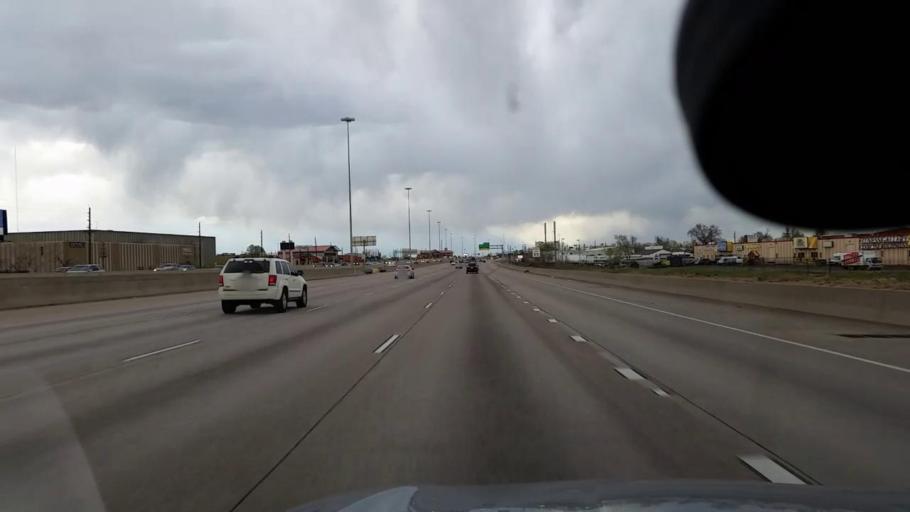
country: US
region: Colorado
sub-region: Adams County
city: Twin Lakes
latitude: 39.7908
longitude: -104.9884
